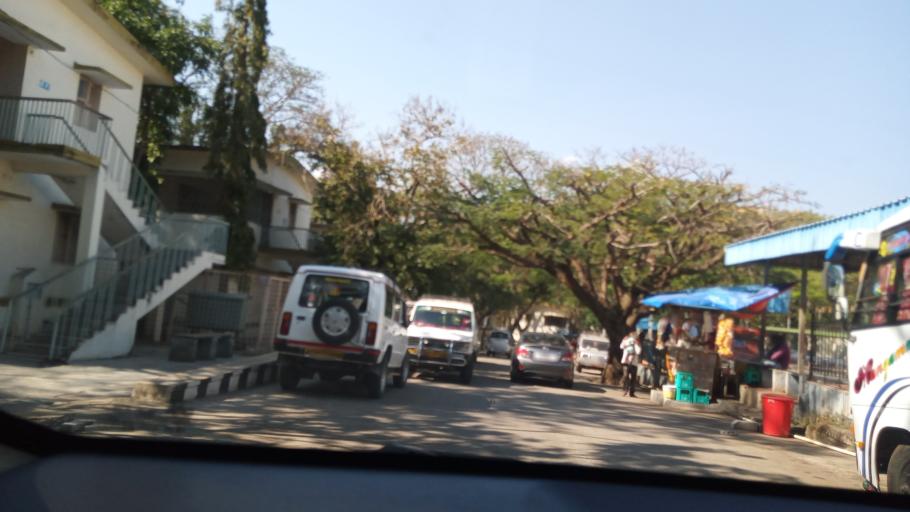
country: IN
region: Andhra Pradesh
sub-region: Chittoor
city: Tirumala
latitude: 13.6769
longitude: 79.3495
